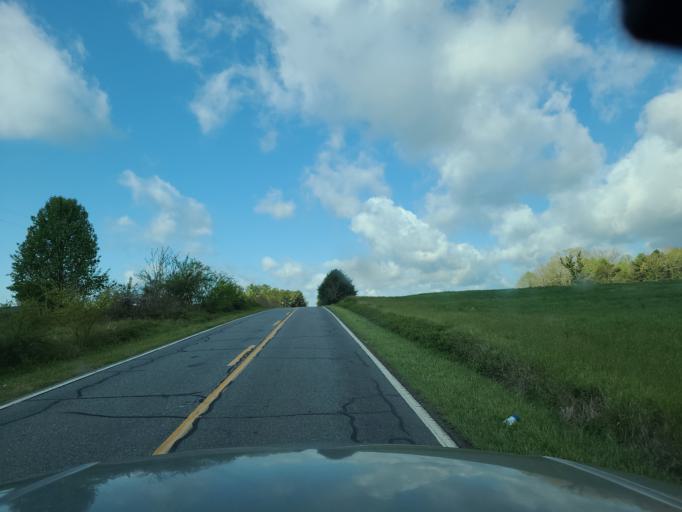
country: US
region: North Carolina
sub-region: Rutherford County
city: Forest City
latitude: 35.4349
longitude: -81.8396
